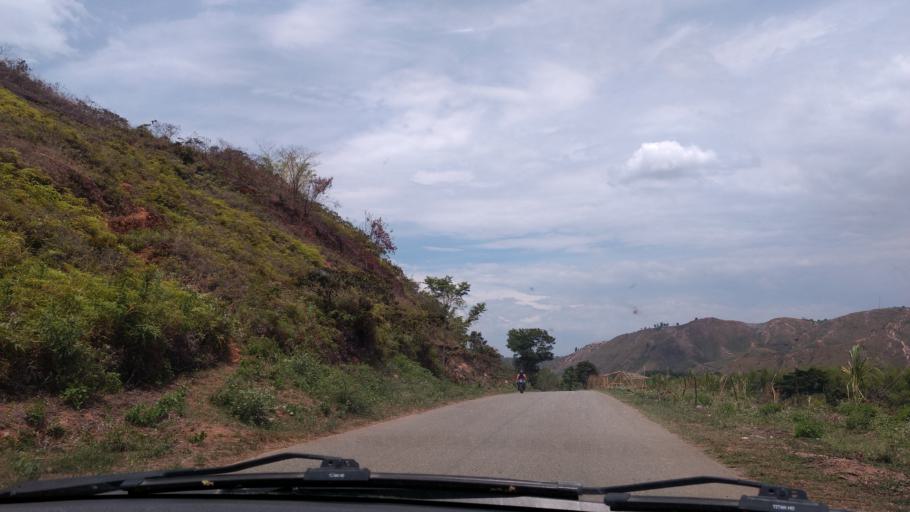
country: CO
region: Cauca
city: Buenos Aires
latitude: 3.0429
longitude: -76.6684
